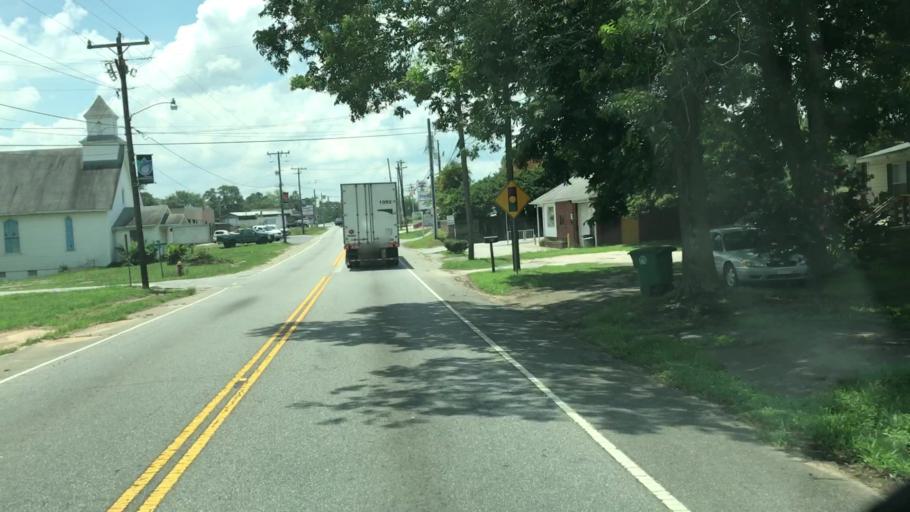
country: US
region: South Carolina
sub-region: Anderson County
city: Williamston
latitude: 34.6242
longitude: -82.4708
